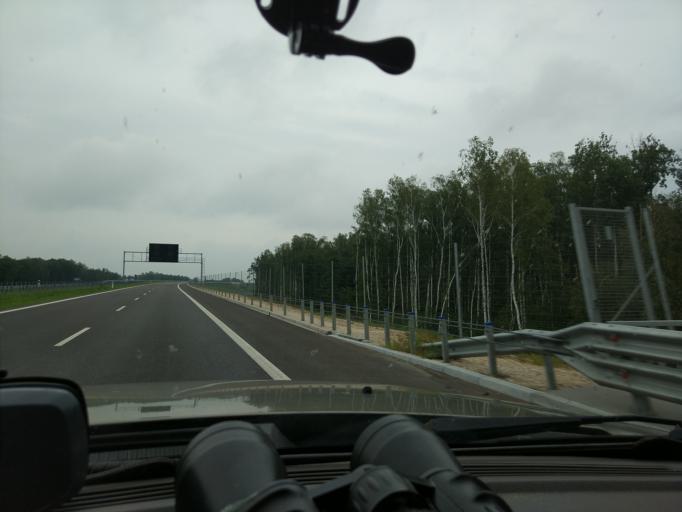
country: PL
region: Podlasie
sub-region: Powiat zambrowski
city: Szumowo
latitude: 52.9387
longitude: 22.1454
